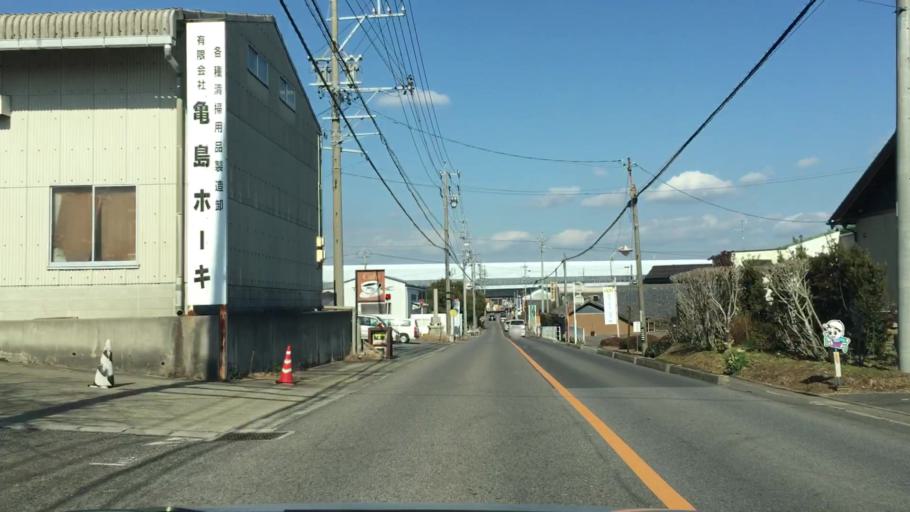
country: JP
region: Aichi
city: Anjo
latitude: 35.0108
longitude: 137.1211
